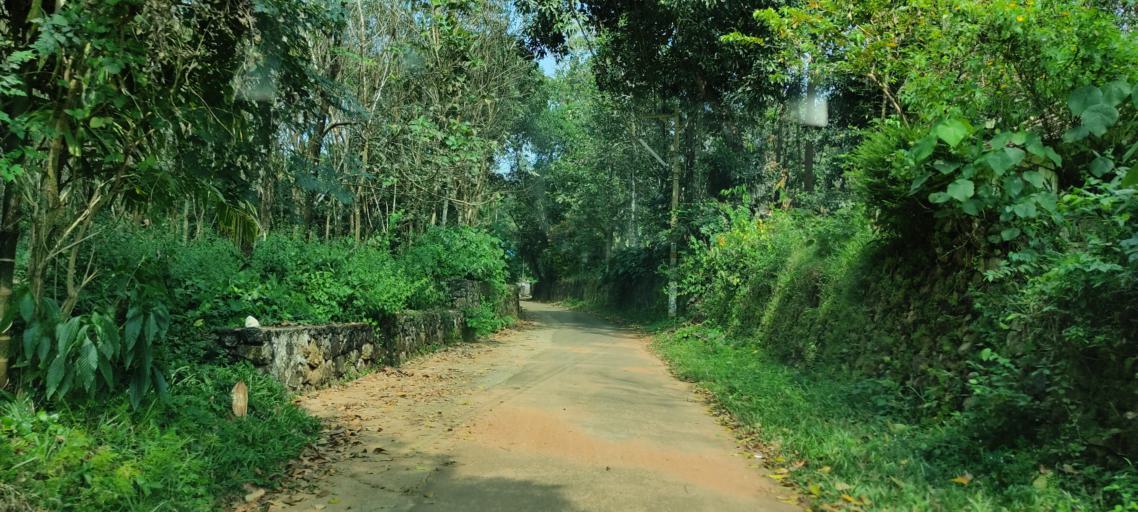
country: IN
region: Kerala
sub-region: Pattanamtitta
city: Adur
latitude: 9.2106
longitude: 76.6946
